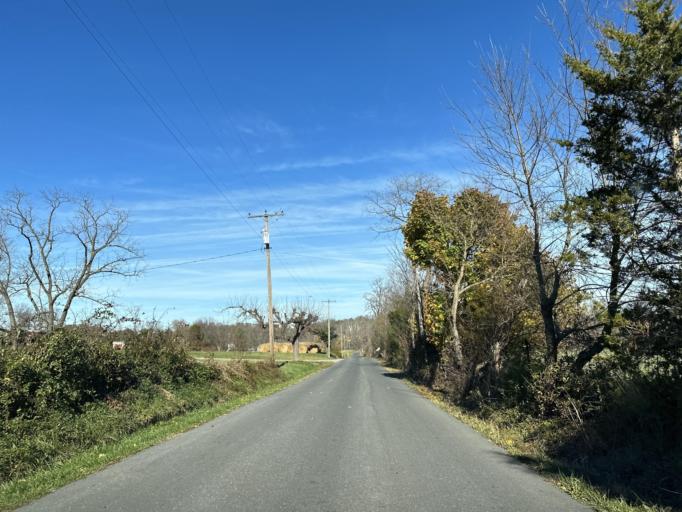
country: US
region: Virginia
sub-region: Augusta County
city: Weyers Cave
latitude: 38.2259
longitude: -78.9247
